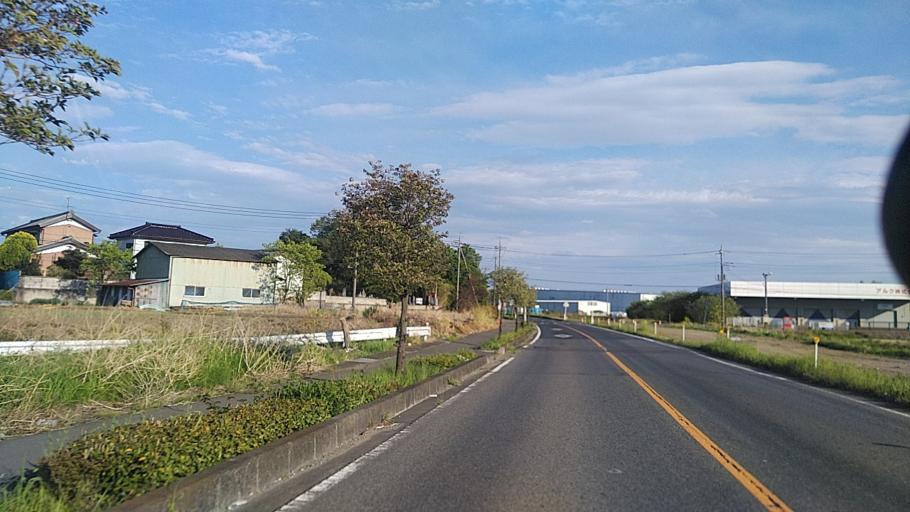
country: JP
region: Gunma
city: Tatebayashi
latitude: 36.2244
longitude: 139.5798
